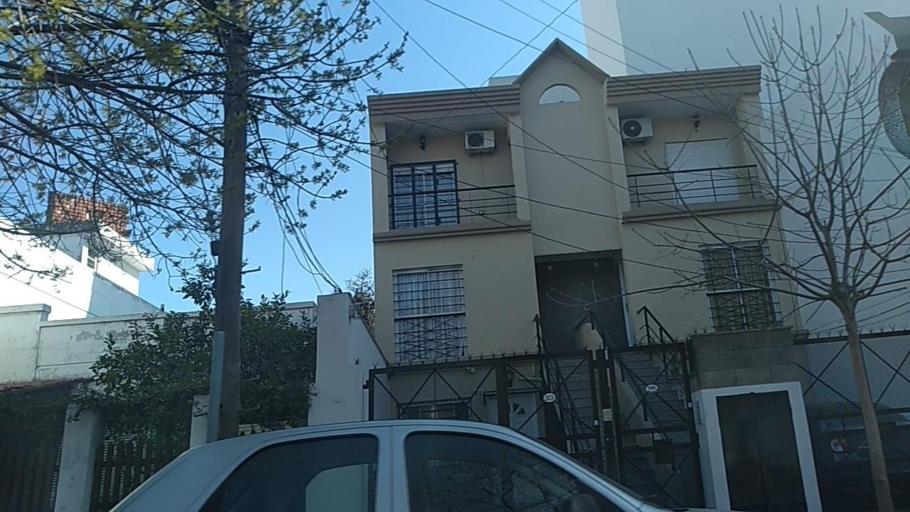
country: AR
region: Buenos Aires F.D.
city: Villa Santa Rita
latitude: -34.6079
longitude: -58.4996
